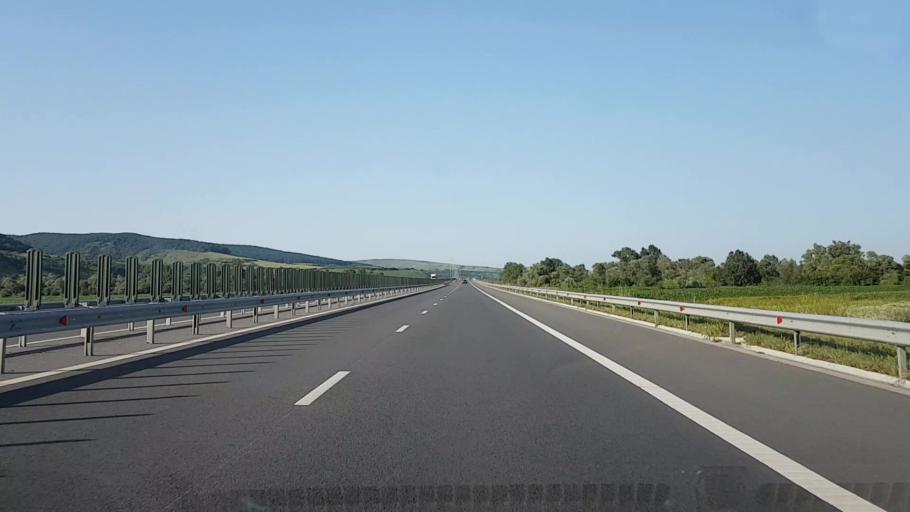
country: RO
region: Alba
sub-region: Comuna Miraslau
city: Miraslau
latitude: 46.3606
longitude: 23.7303
